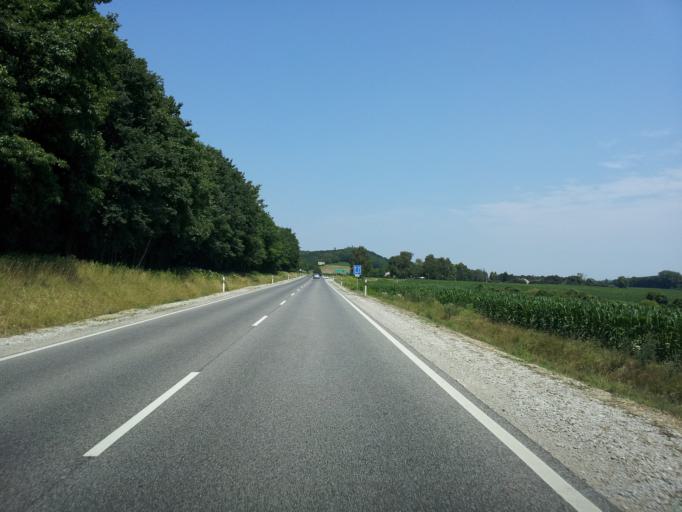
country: HU
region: Zala
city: Zalaegerszeg
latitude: 46.8346
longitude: 16.9285
